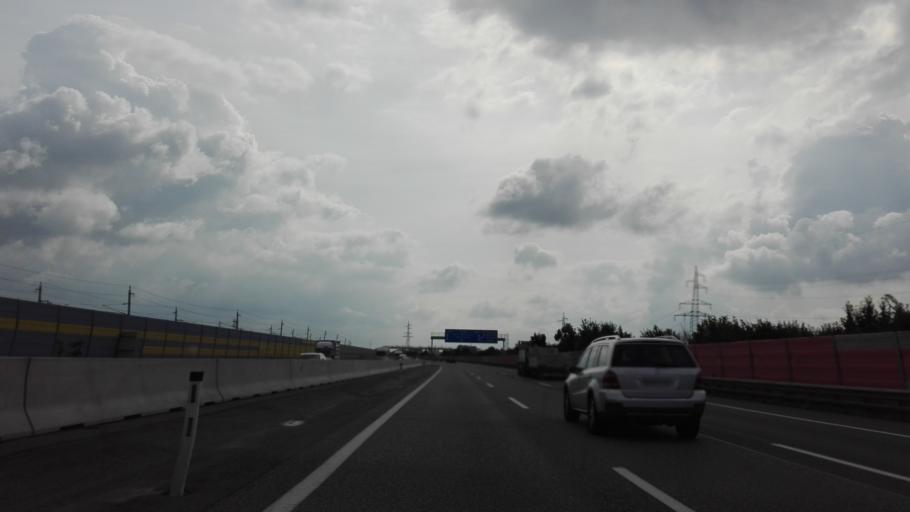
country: AT
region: Lower Austria
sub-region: Sankt Polten Stadt
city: Sankt Poelten
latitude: 48.1760
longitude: 15.6378
